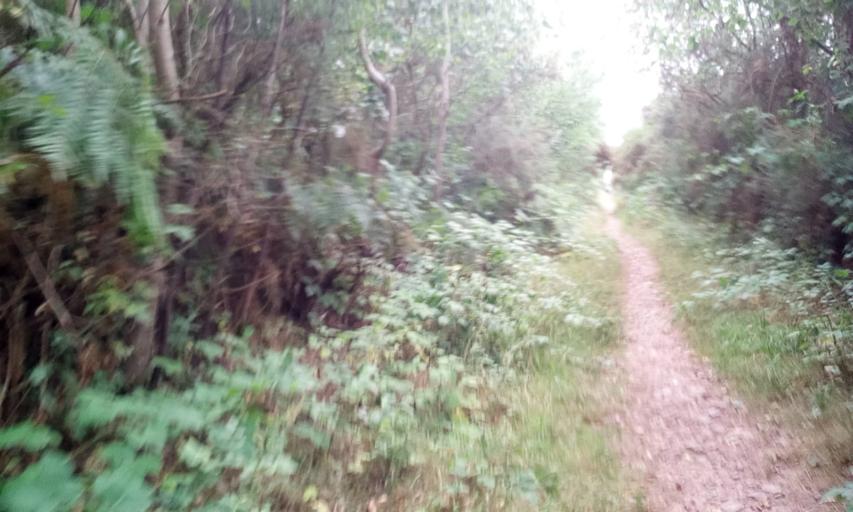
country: FR
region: Lower Normandy
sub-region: Departement du Calvados
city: Mouen
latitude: 49.1405
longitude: -0.4805
